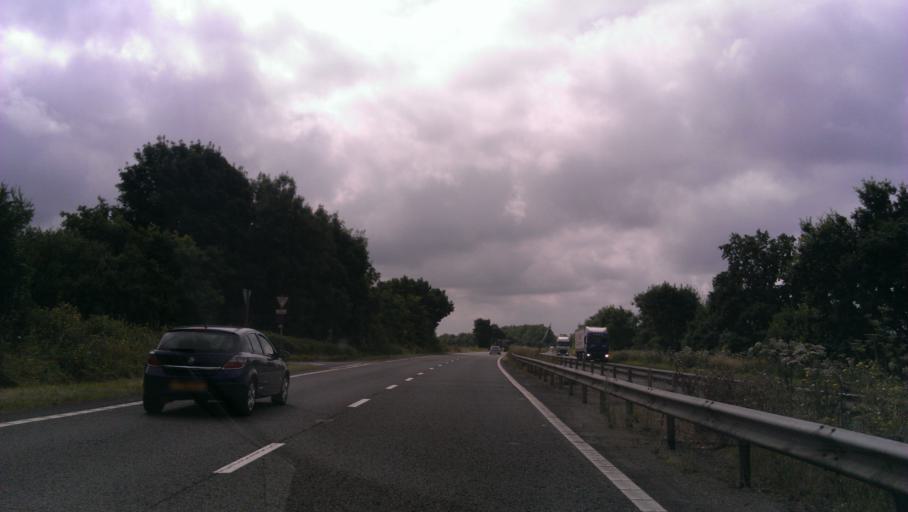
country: GB
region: England
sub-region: Kent
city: Wootton
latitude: 51.1921
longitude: 1.1871
